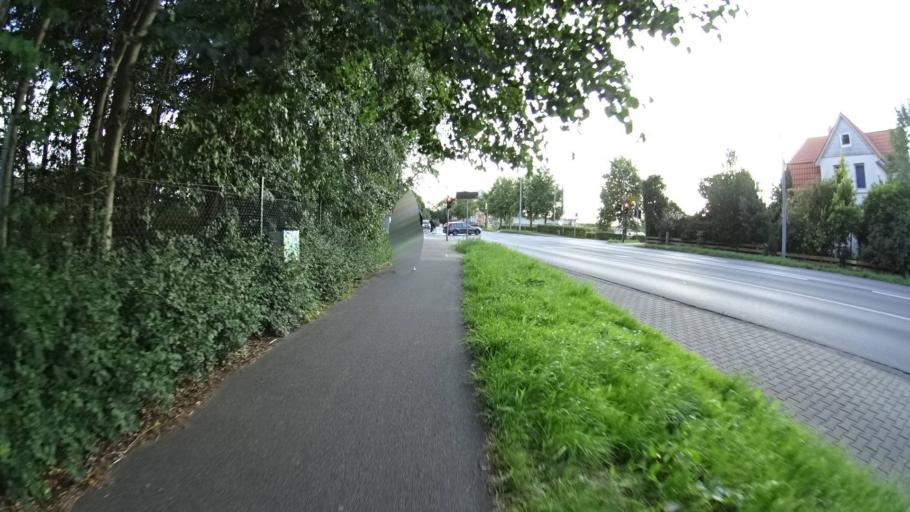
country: DE
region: Lower Saxony
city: Lueneburg
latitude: 53.2216
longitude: 10.3868
